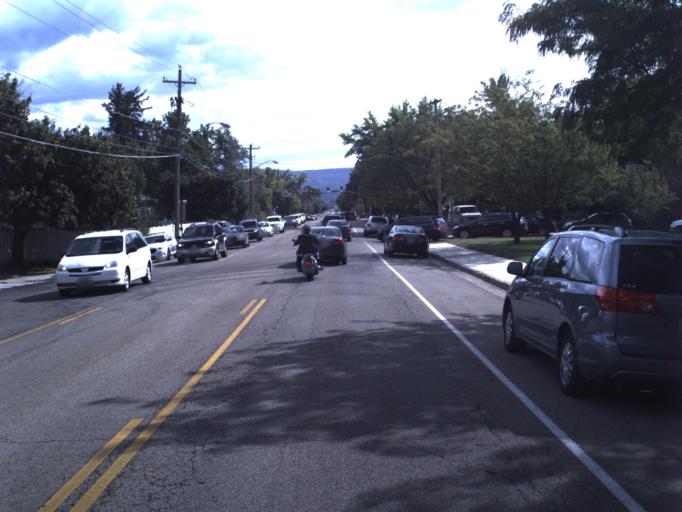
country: US
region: Utah
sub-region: Davis County
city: Centerville
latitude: 40.9308
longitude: -111.8790
